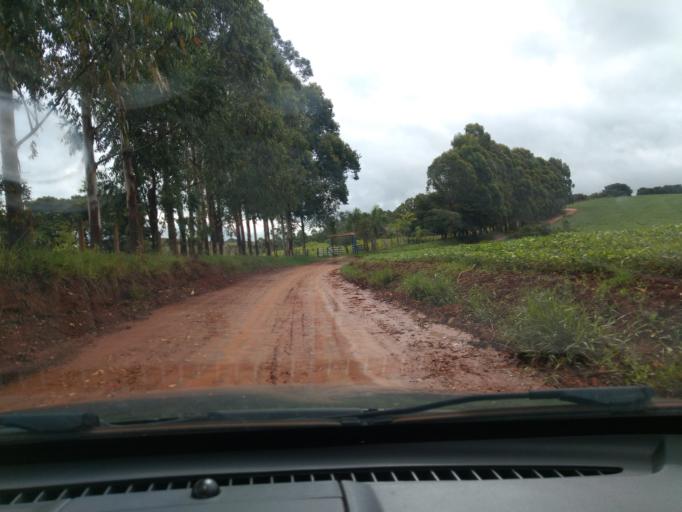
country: BR
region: Minas Gerais
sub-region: Lavras
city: Lavras
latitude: -21.5084
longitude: -44.9212
